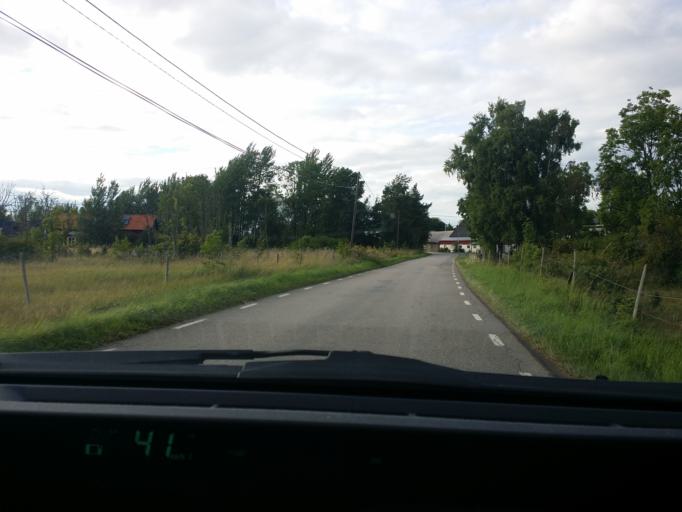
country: SE
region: Kalmar
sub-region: Borgholms Kommun
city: Borgholm
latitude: 57.1170
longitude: 16.9665
